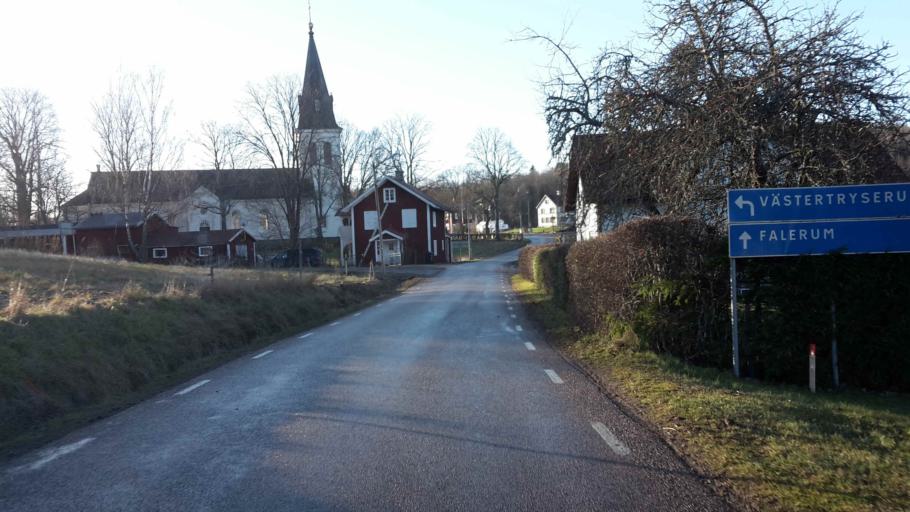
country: SE
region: Kalmar
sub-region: Vasterviks Kommun
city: Overum
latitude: 58.1537
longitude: 16.3278
